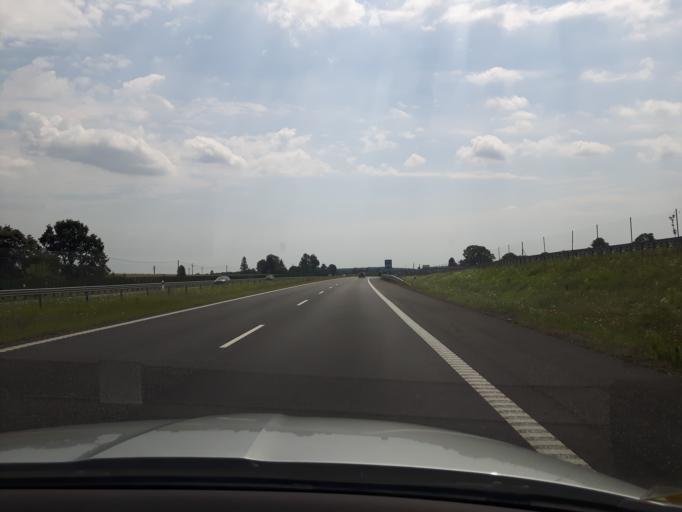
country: PL
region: Warmian-Masurian Voivodeship
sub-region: Powiat olsztynski
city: Olsztynek
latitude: 53.4859
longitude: 20.3203
